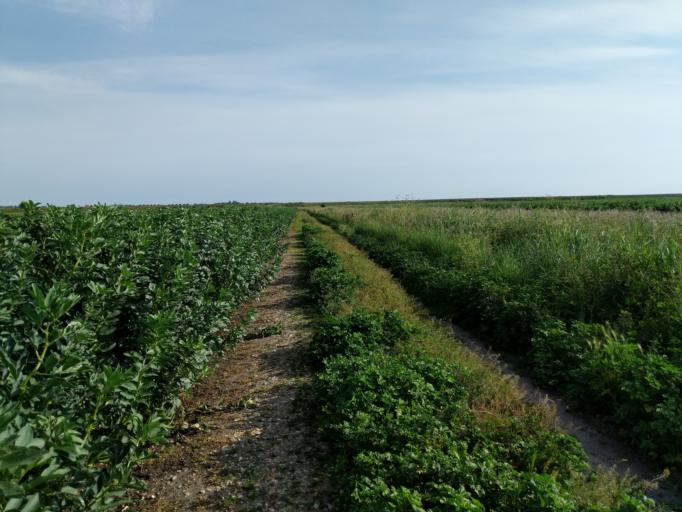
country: GB
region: England
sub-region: Kent
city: Faversham
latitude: 51.3402
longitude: 0.9105
